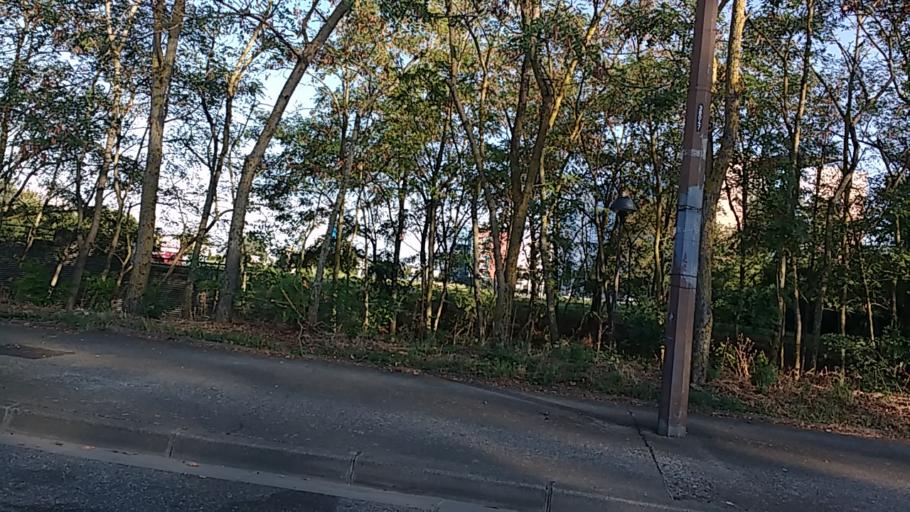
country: FR
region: Midi-Pyrenees
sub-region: Departement de la Haute-Garonne
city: Cugnaux
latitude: 43.5678
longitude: 1.3763
